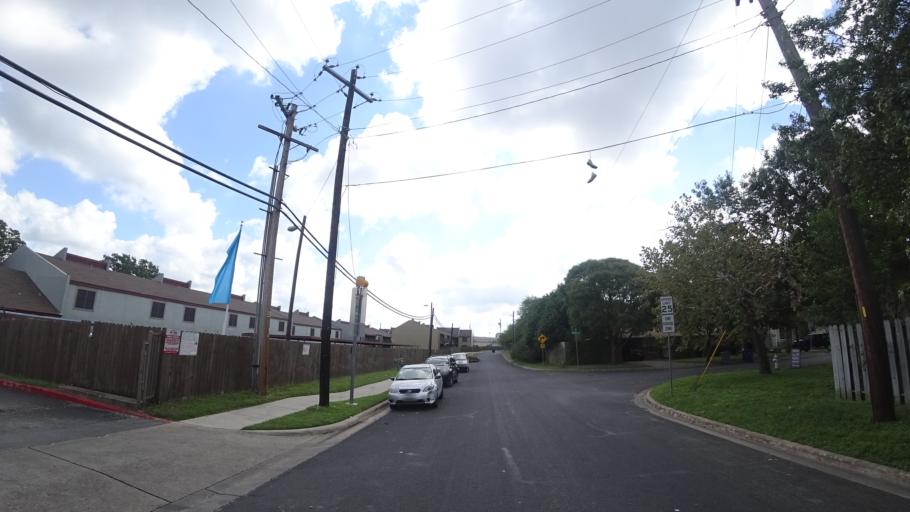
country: US
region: Texas
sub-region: Travis County
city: Austin
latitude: 30.3541
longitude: -97.7174
